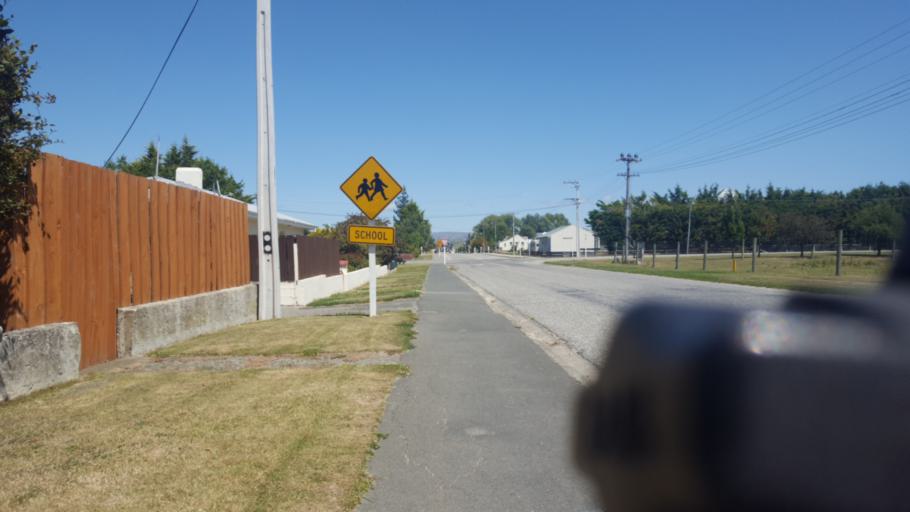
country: NZ
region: Otago
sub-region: Dunedin City
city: Dunedin
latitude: -45.1257
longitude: 170.1017
